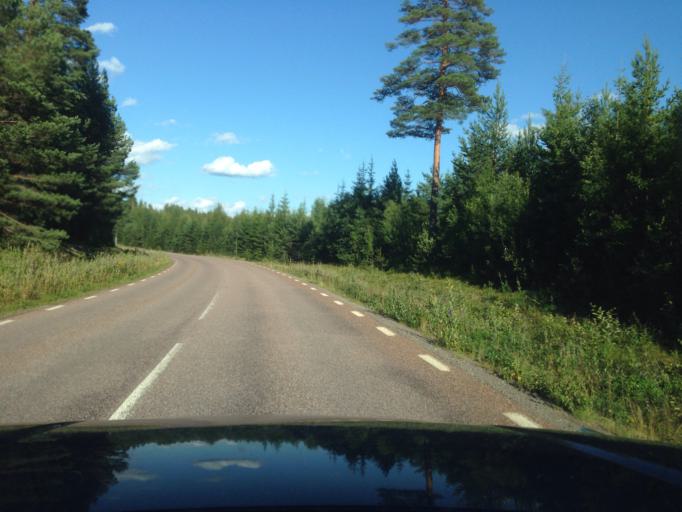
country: SE
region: Dalarna
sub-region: Ludvika Kommun
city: Grangesberg
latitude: 60.1281
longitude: 15.0192
